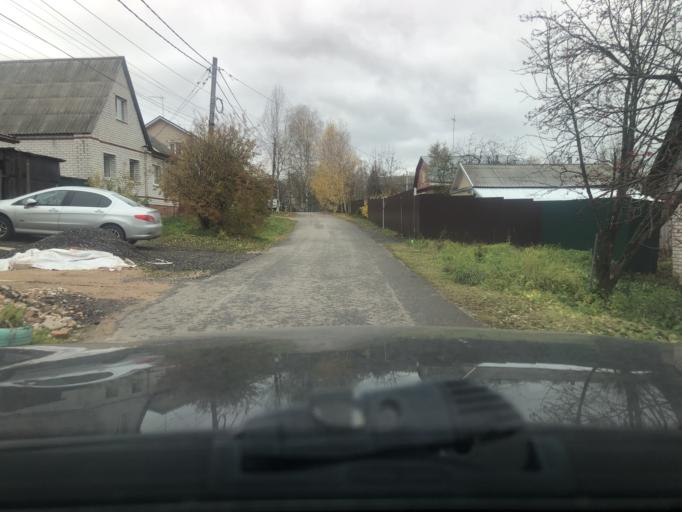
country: RU
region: Moskovskaya
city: Sergiyev Posad
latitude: 56.3175
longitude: 38.1267
